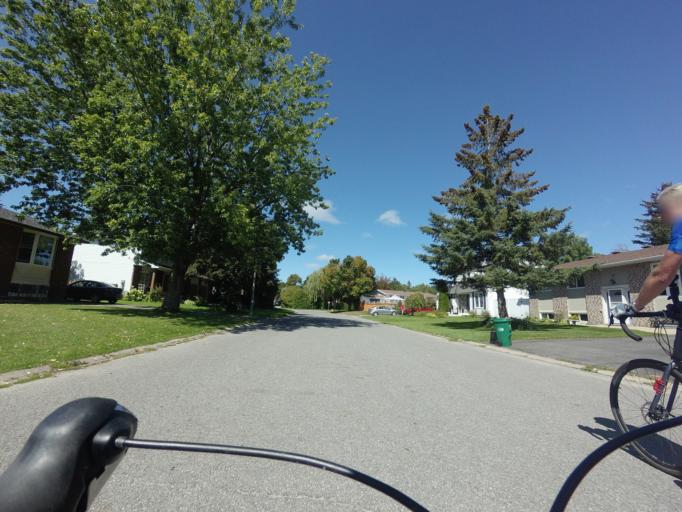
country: CA
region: Ontario
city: Bells Corners
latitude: 45.1911
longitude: -75.8257
